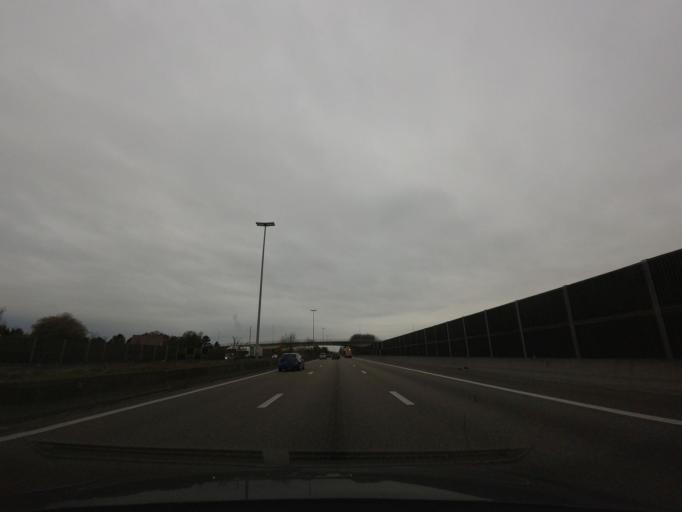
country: BE
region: Flanders
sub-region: Provincie Oost-Vlaanderen
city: Laarne
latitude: 51.0629
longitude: 3.8694
